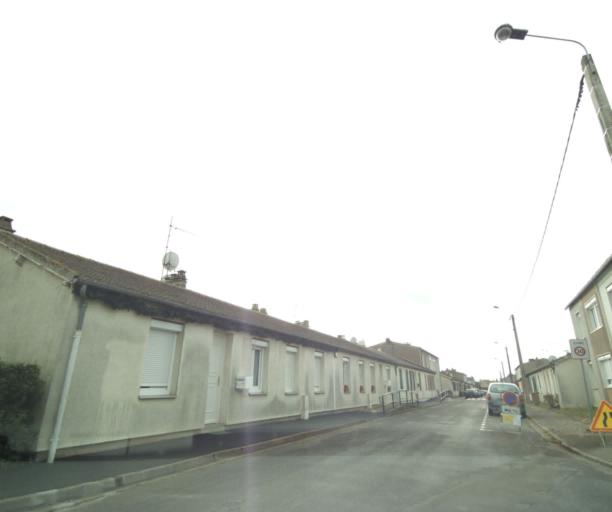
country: FR
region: Centre
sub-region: Departement d'Eure-et-Loir
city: Dreux
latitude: 48.7463
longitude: 1.3409
